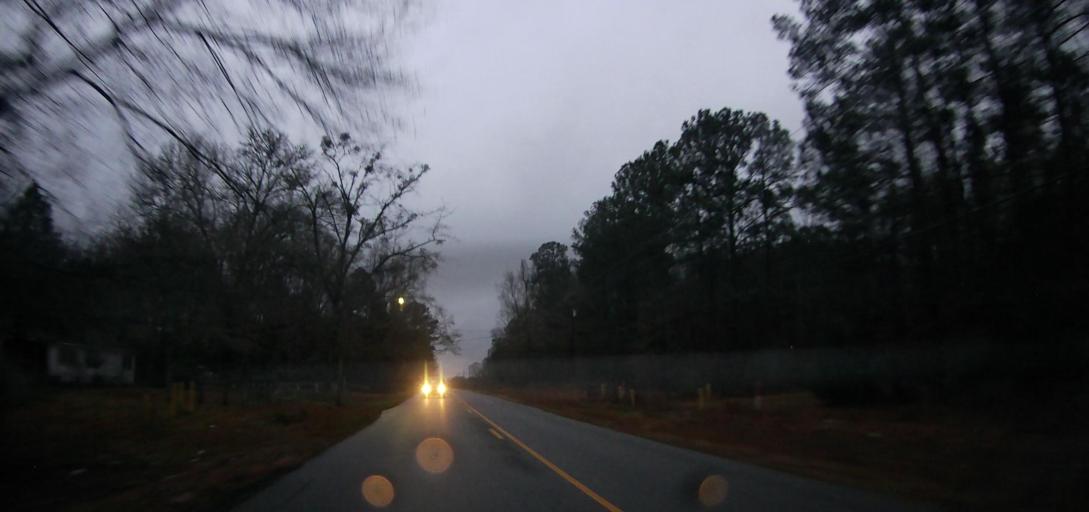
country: US
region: Alabama
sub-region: Tuscaloosa County
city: Vance
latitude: 33.1507
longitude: -87.2299
